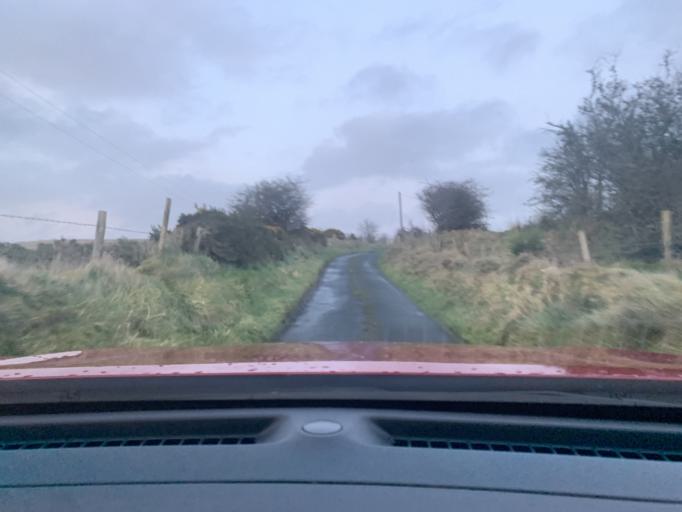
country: IE
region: Connaught
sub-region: Sligo
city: Ballymote
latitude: 54.0500
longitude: -8.4012
